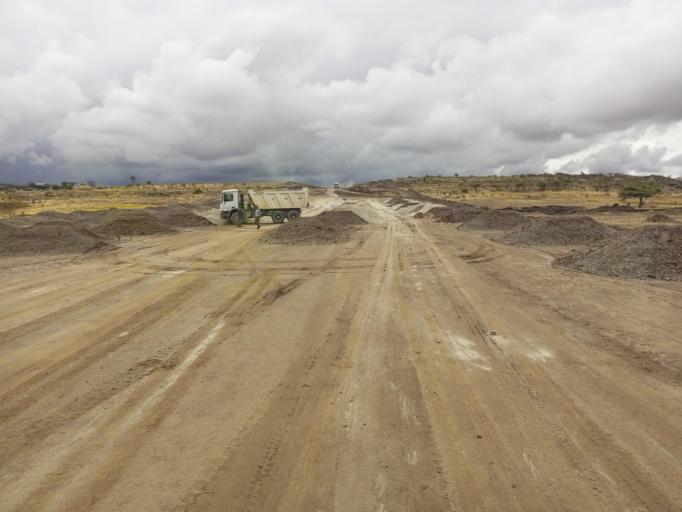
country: ET
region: Oromiya
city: Shashemene
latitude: 7.4875
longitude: 38.6807
